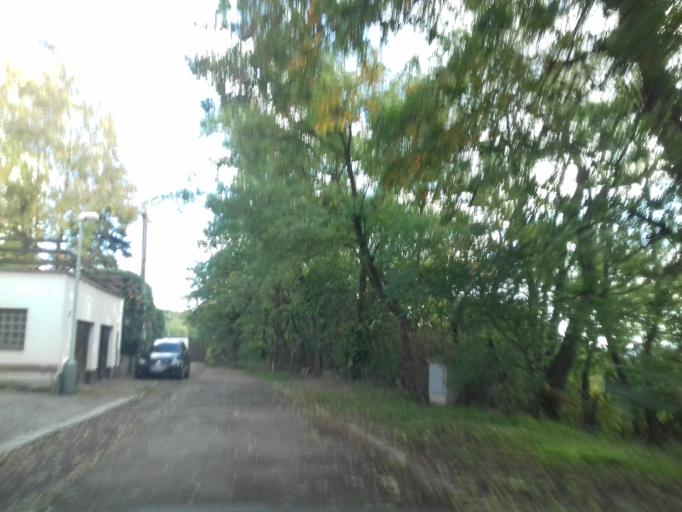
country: CZ
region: Praha
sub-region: Praha 4
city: Hodkovicky
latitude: 50.0253
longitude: 14.4076
